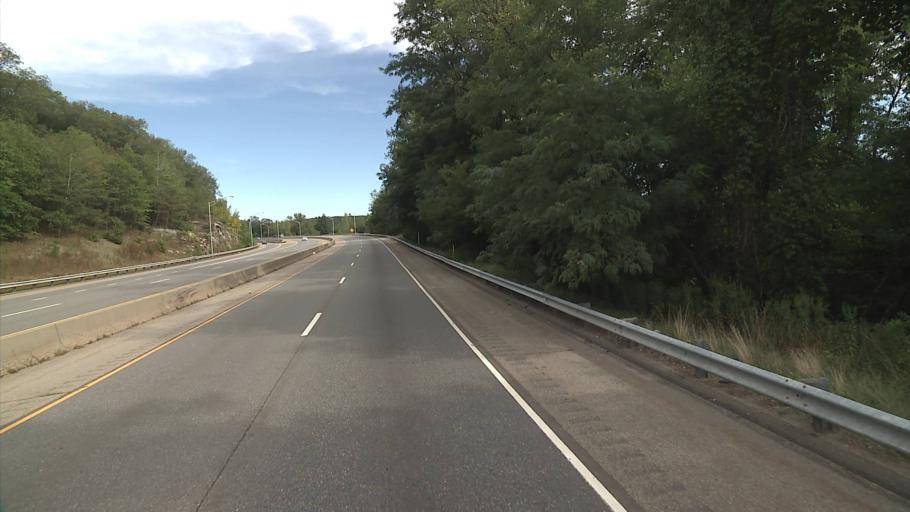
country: US
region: Connecticut
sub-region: New London County
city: Norwich
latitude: 41.5533
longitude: -72.1174
